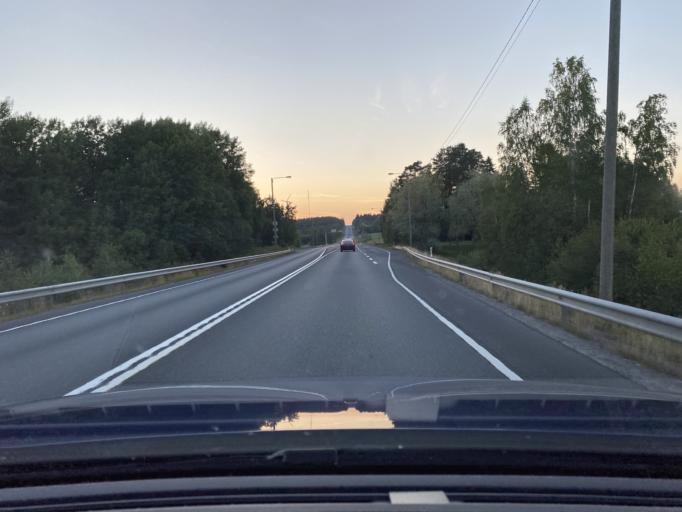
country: FI
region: Pirkanmaa
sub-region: Luoteis-Pirkanmaa
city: Ikaalinen
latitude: 61.7726
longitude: 23.0111
